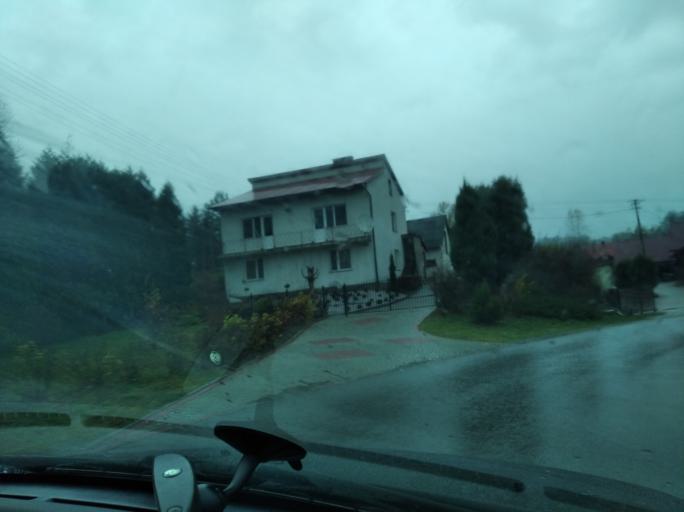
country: PL
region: Subcarpathian Voivodeship
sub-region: Powiat rzeszowski
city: Chmielnik
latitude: 49.9760
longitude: 22.1674
